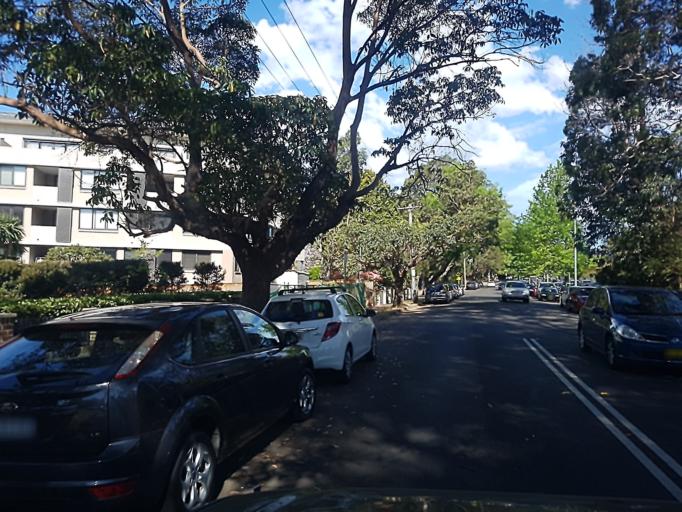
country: AU
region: New South Wales
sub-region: Ku-ring-gai
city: North Wahroonga
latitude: -33.7152
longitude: 151.1146
